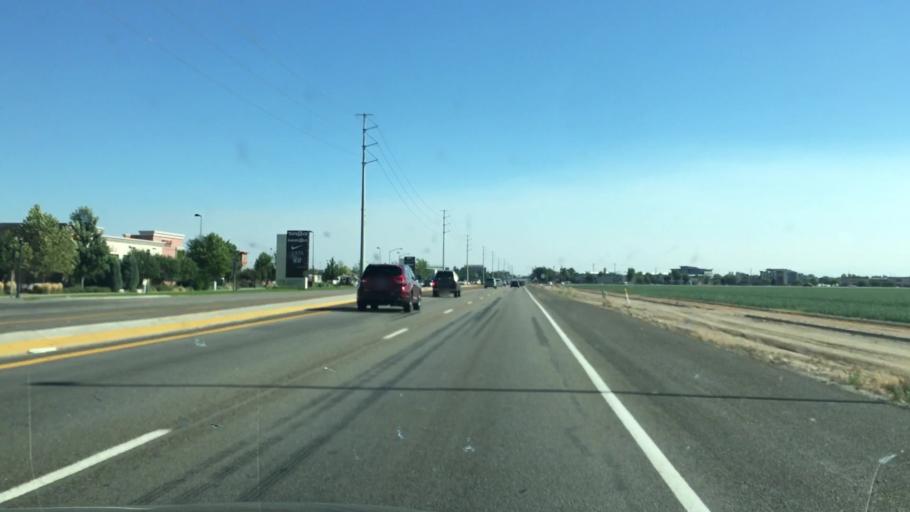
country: US
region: Idaho
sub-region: Ada County
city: Meridian
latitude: 43.6253
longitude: -116.3547
